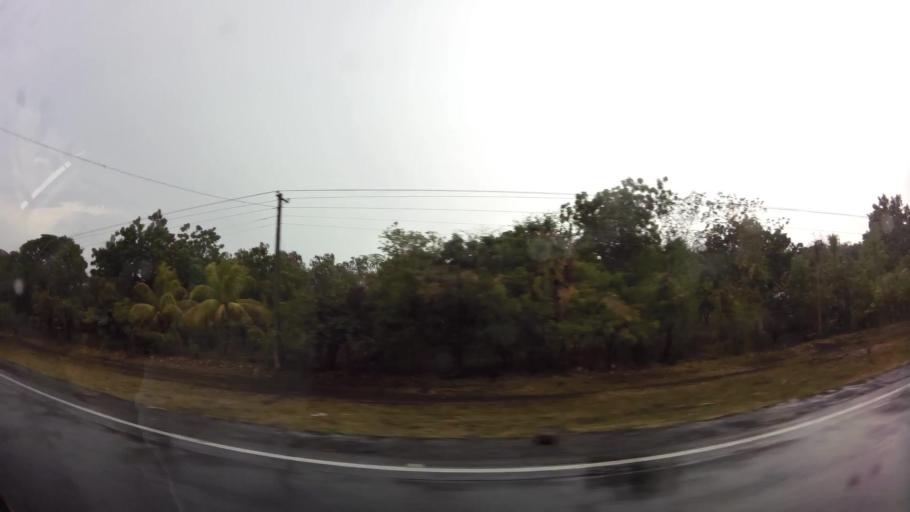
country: NI
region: Leon
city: Telica
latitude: 12.5357
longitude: -86.8450
